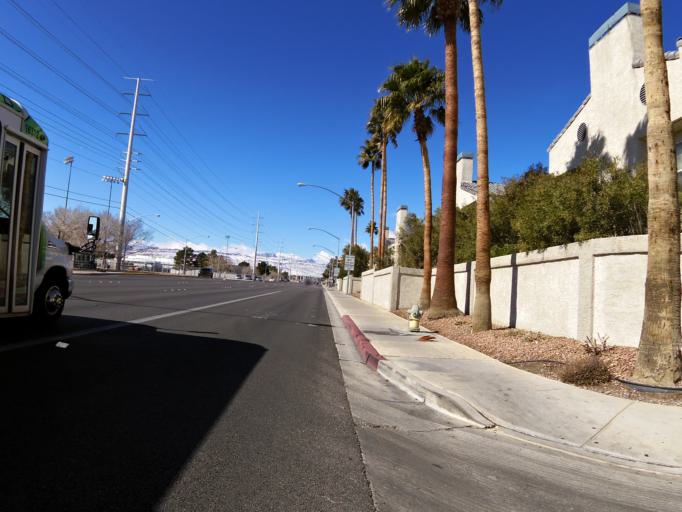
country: US
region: Nevada
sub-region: Clark County
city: Spring Valley
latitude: 36.1147
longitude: -115.2283
